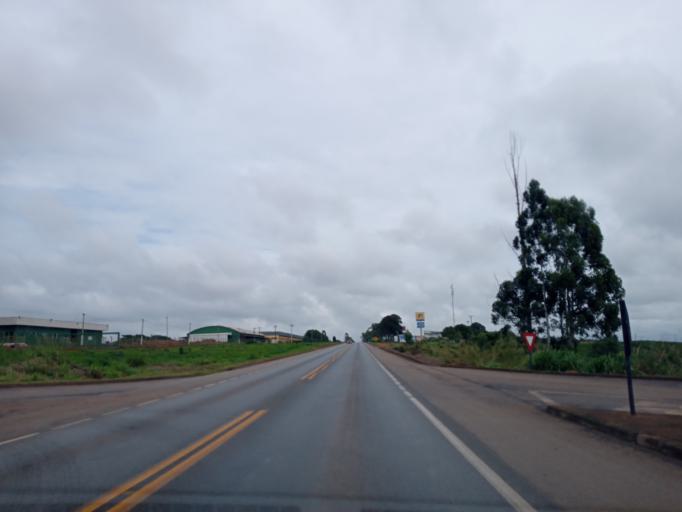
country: BR
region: Minas Gerais
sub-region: Campos Altos
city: Campos Altos
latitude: -19.6594
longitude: -46.2086
